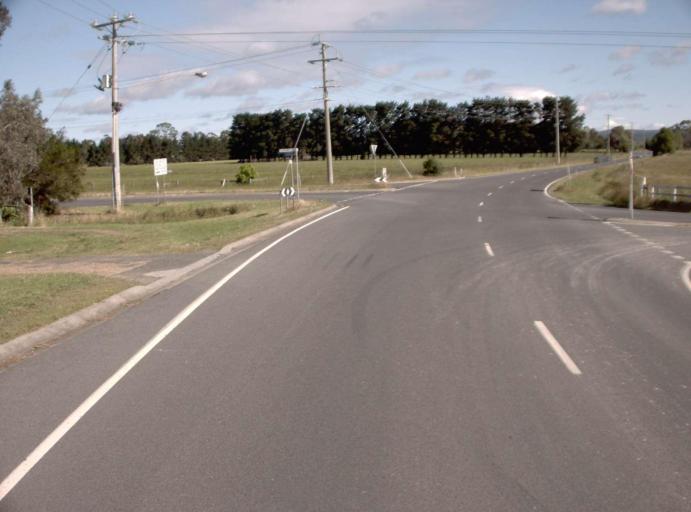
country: AU
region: Victoria
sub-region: Latrobe
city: Traralgon
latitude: -38.1824
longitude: 146.5004
